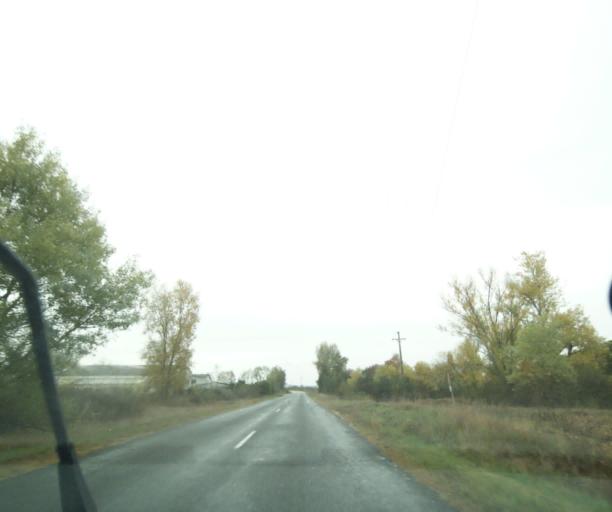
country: FR
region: Rhone-Alpes
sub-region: Departement de l'Ain
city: Loyettes
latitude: 45.7936
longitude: 5.2104
